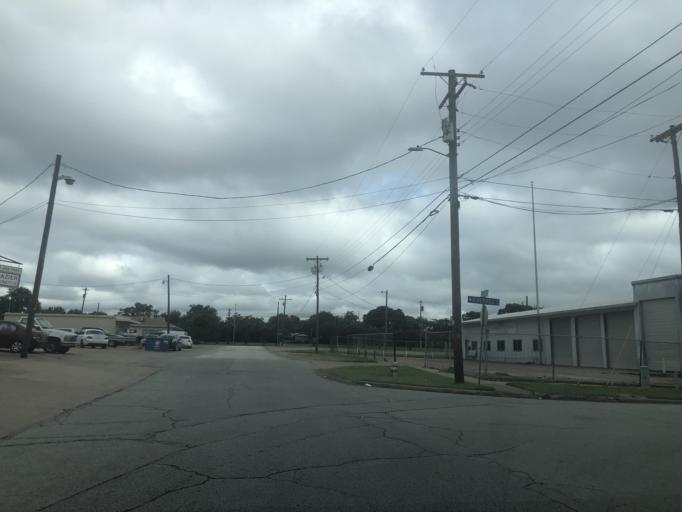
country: US
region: Texas
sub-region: Dallas County
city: Duncanville
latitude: 32.6590
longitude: -96.9059
